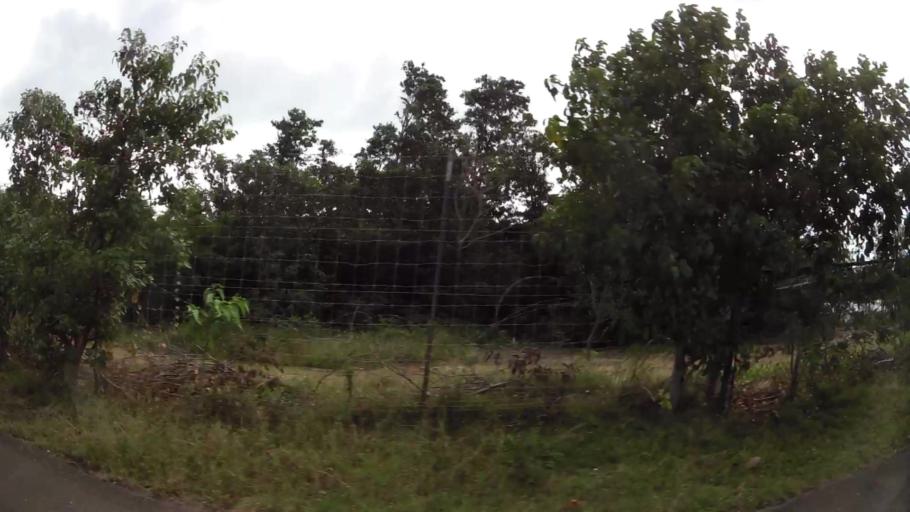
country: AG
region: Saint John
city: Saint John's
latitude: 17.1200
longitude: -61.8901
